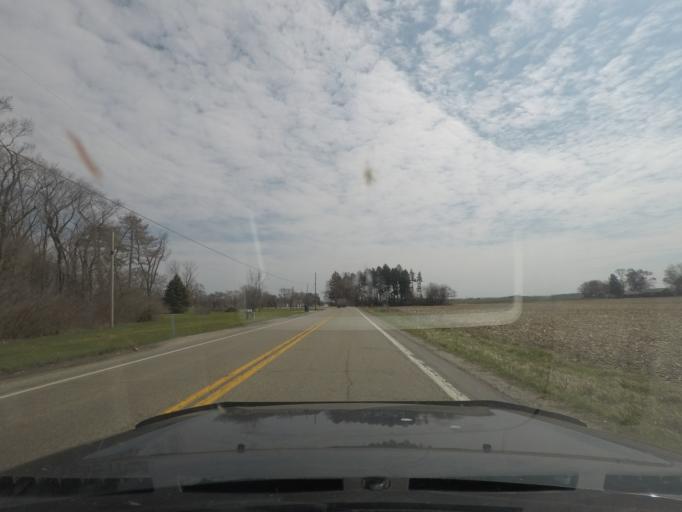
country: US
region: Indiana
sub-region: LaPorte County
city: Kingsford Heights
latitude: 41.4787
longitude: -86.6785
